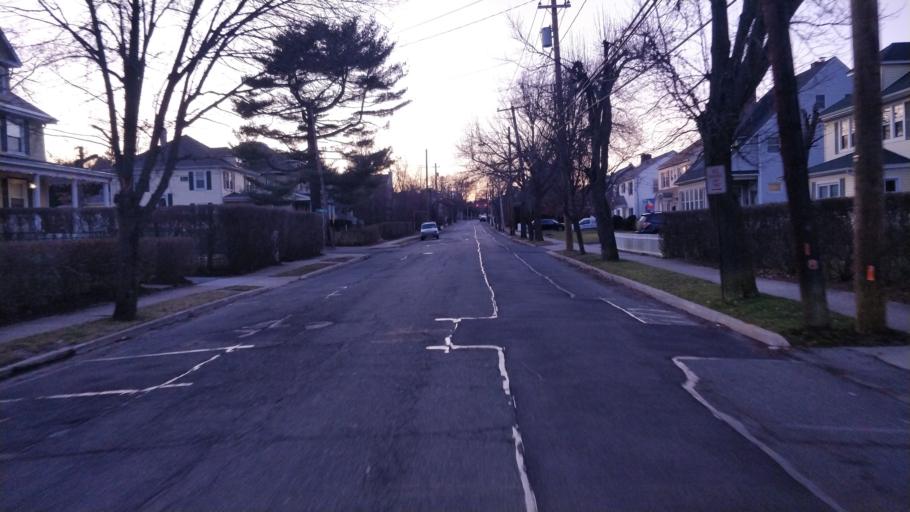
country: US
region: New York
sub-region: Nassau County
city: Glen Cove
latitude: 40.8679
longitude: -73.6377
